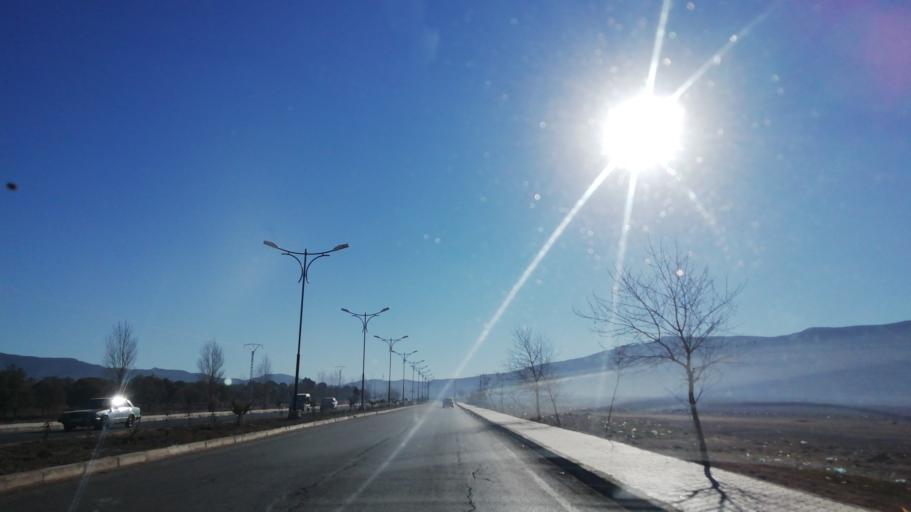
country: DZ
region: El Bayadh
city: El Bayadh
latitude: 33.6644
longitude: 1.0501
